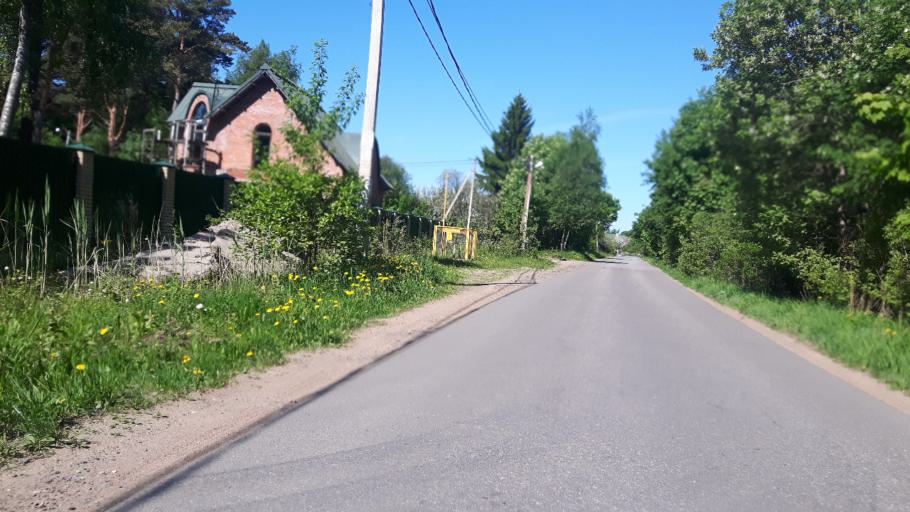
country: RU
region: Leningrad
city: Lebyazh'ye
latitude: 59.9707
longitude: 29.3849
